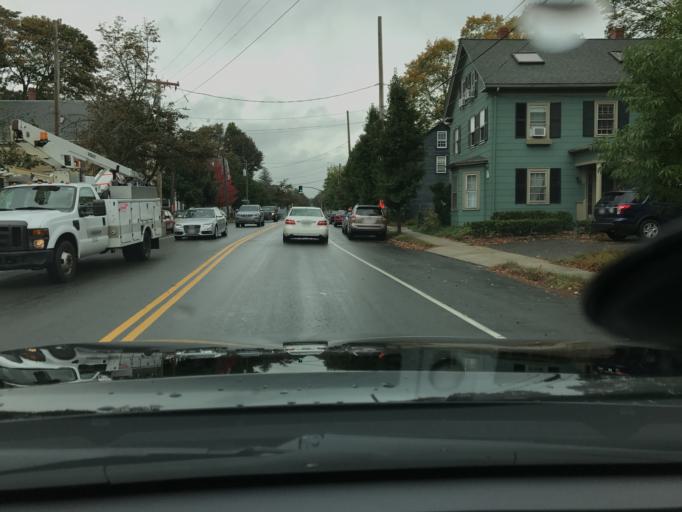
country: US
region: Massachusetts
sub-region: Essex County
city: Salem
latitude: 42.5291
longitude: -70.9045
